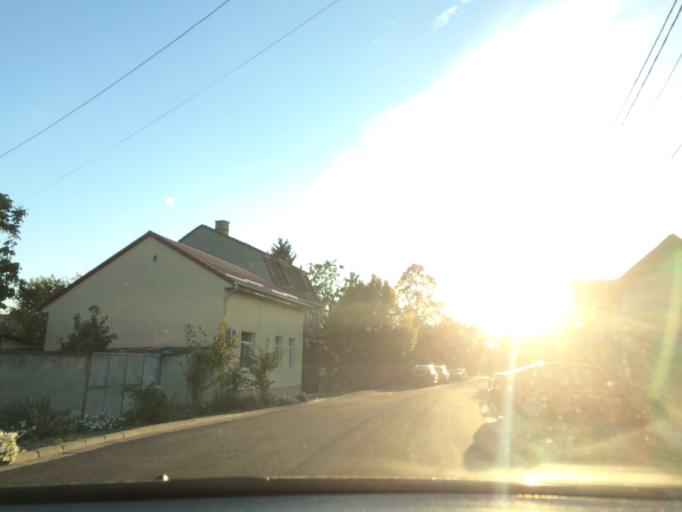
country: RO
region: Timis
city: Timisoara
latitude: 45.7602
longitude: 21.2006
